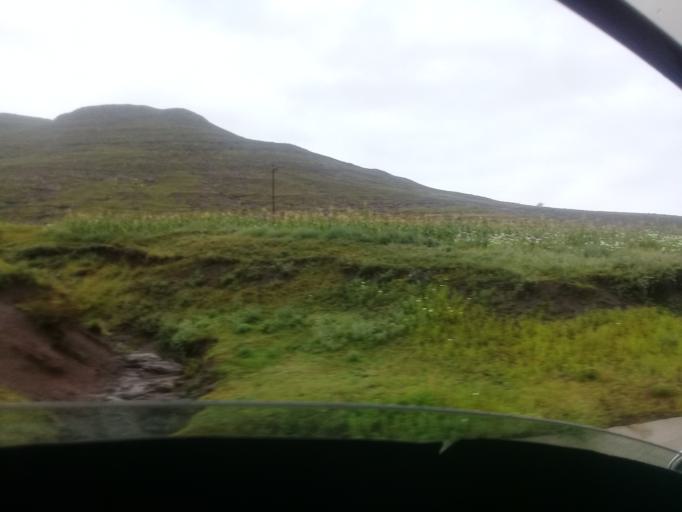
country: LS
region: Mokhotlong
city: Mokhotlong
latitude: -29.3303
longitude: 29.0291
